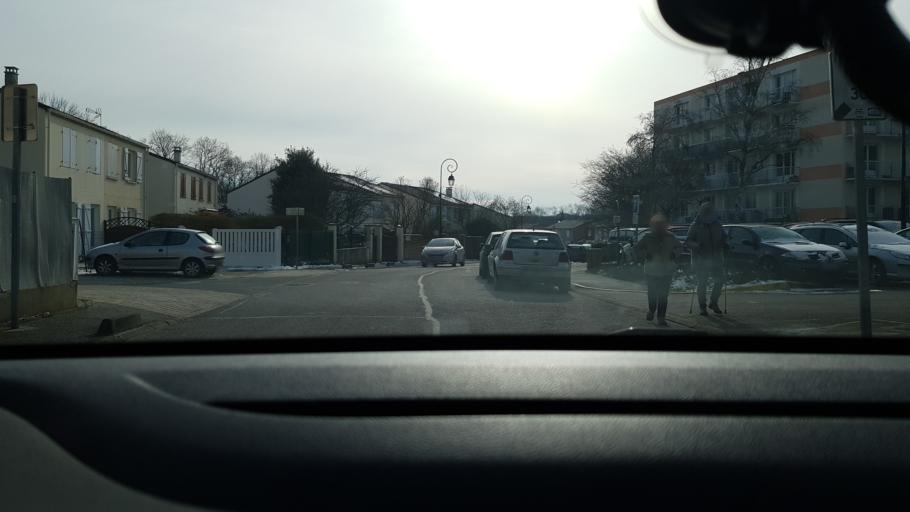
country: FR
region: Ile-de-France
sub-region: Departement de l'Essonne
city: Villiers-le-Bacle
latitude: 48.7173
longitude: 2.1045
